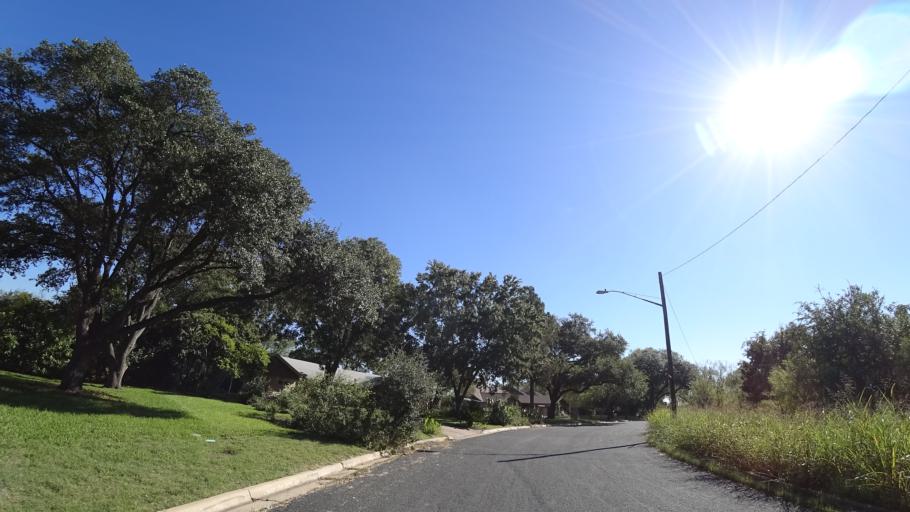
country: US
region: Texas
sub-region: Travis County
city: Austin
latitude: 30.2295
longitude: -97.7100
